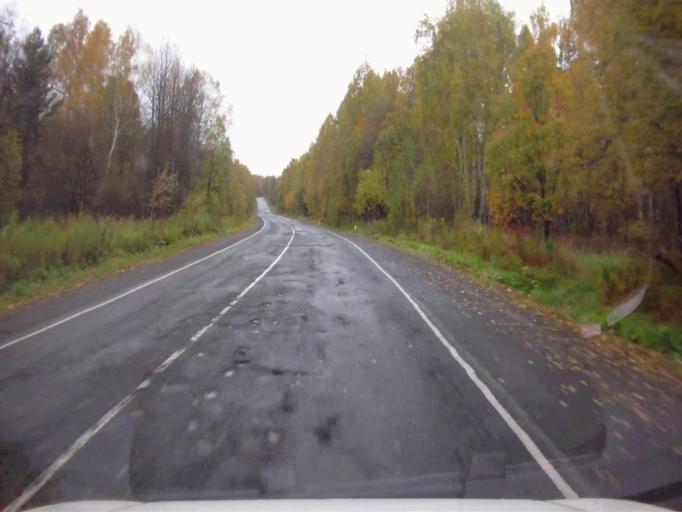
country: RU
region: Chelyabinsk
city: Nizhniy Ufaley
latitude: 56.0548
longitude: 60.0507
